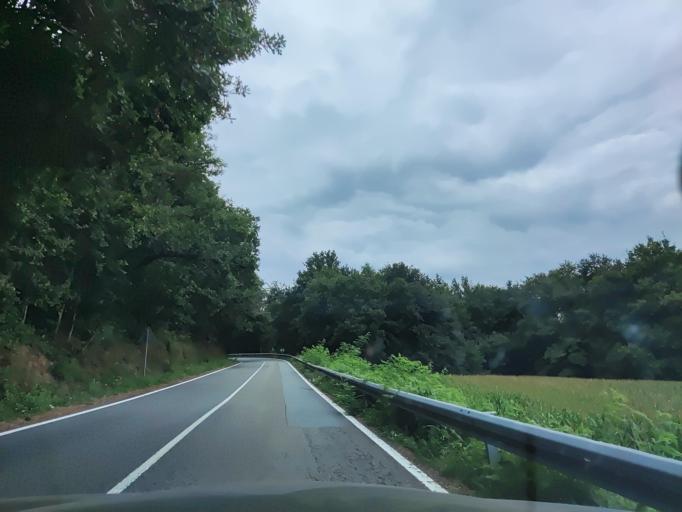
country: ES
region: Galicia
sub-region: Provincia da Coruna
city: Teo
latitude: 42.7636
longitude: -8.5558
